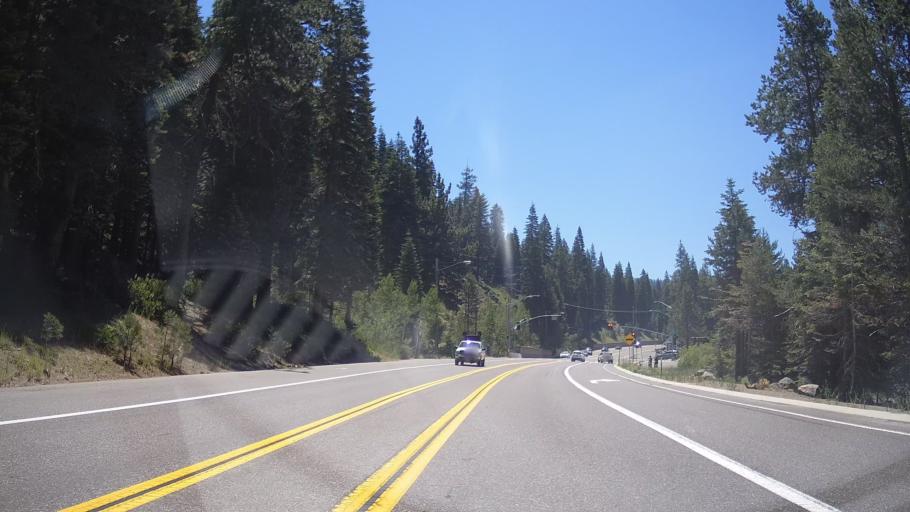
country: US
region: California
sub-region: Placer County
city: Sunnyside-Tahoe City
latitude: 39.1881
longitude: -120.1958
